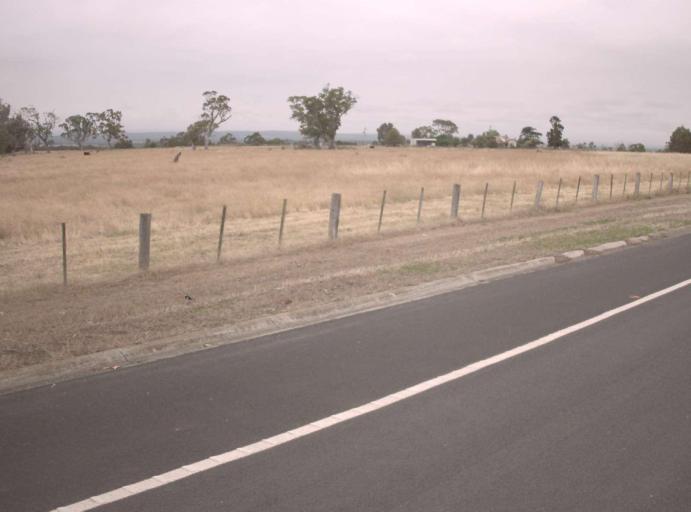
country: AU
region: Victoria
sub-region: Wellington
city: Heyfield
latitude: -38.1366
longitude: 146.7974
